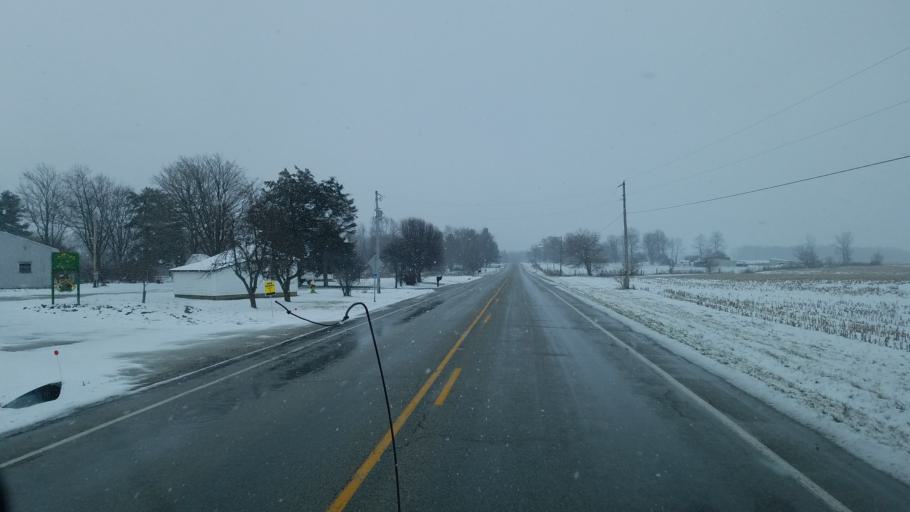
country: US
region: Indiana
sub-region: Randolph County
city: Lynn
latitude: 39.9358
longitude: -84.9749
